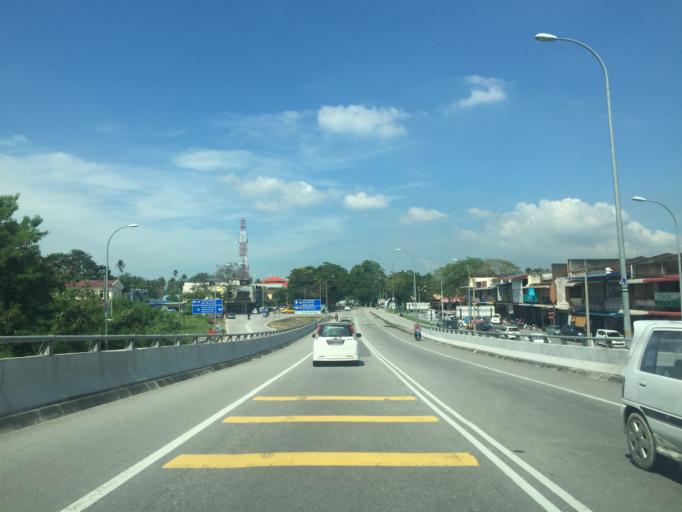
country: MY
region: Penang
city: Tasek Glugor
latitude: 5.4806
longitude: 100.4962
